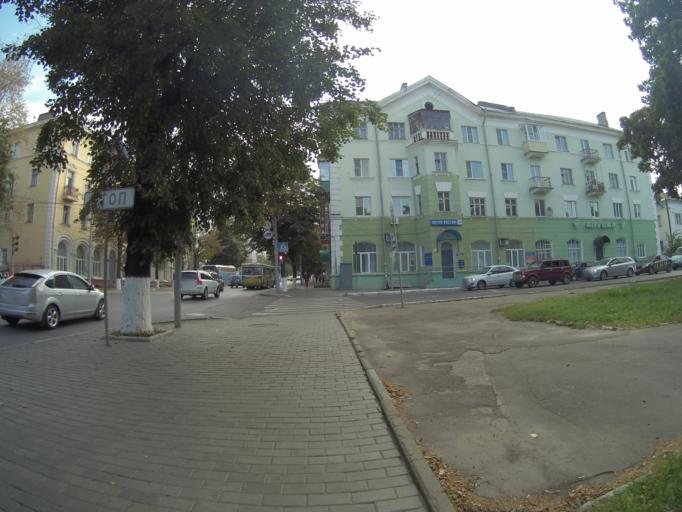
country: RU
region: Vladimir
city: Vladimir
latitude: 56.1339
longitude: 40.4203
